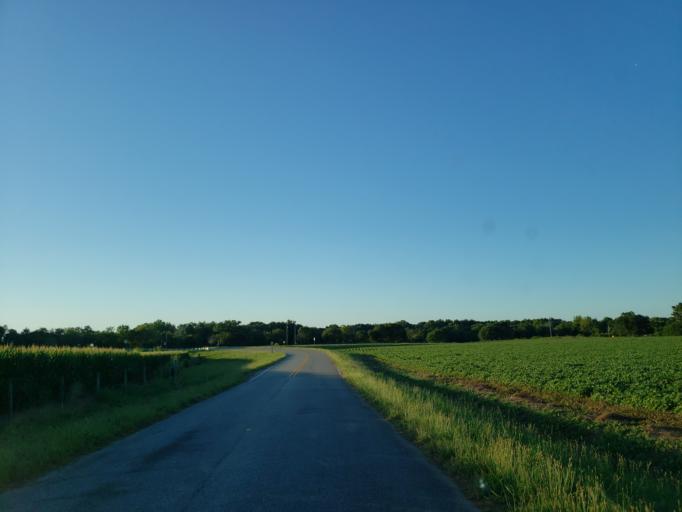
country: US
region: Georgia
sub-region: Bartow County
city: Euharlee
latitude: 34.0906
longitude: -84.9598
